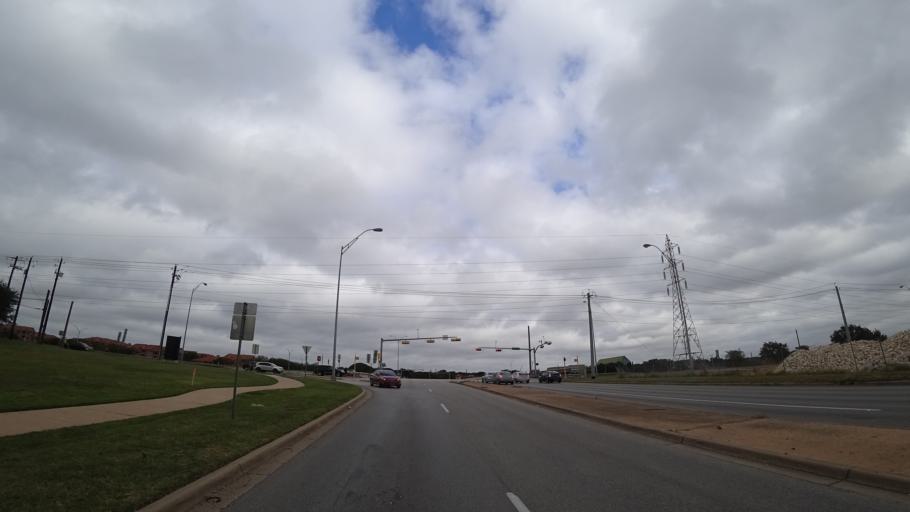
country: US
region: Texas
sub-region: Travis County
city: Wells Branch
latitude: 30.4074
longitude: -97.7158
